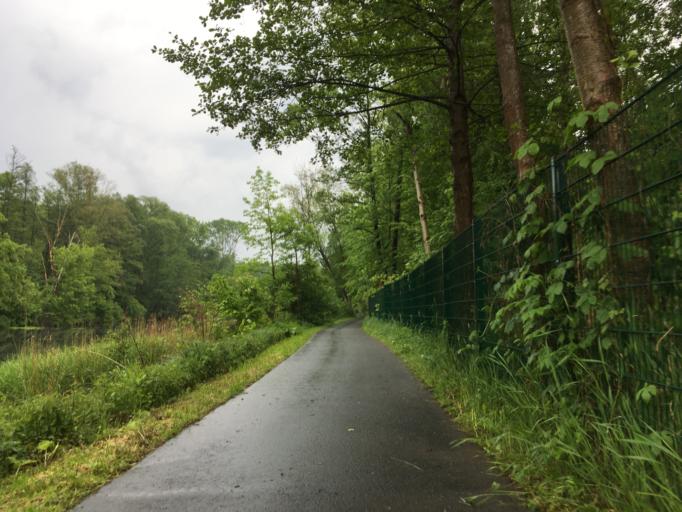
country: DE
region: Brandenburg
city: Eberswalde
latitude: 52.8459
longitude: 13.7779
